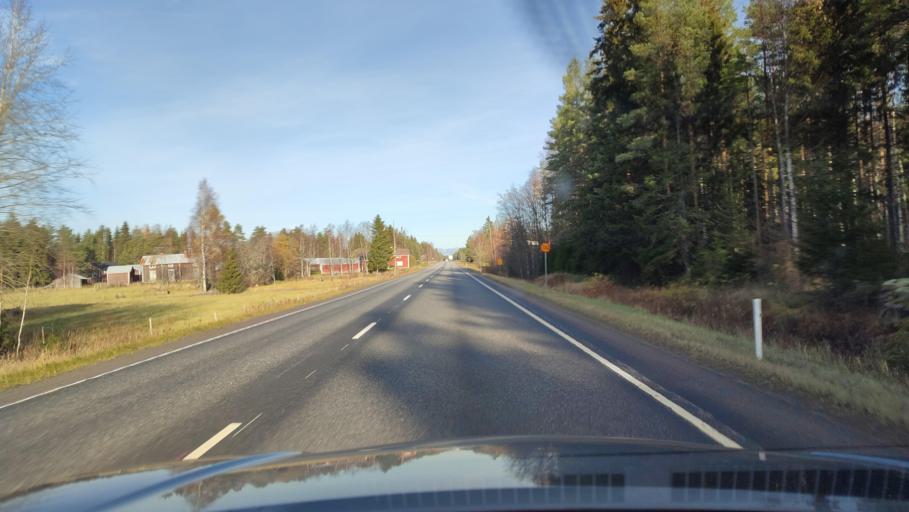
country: FI
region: Ostrobothnia
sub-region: Vaasa
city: Malax
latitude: 62.8203
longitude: 21.6876
